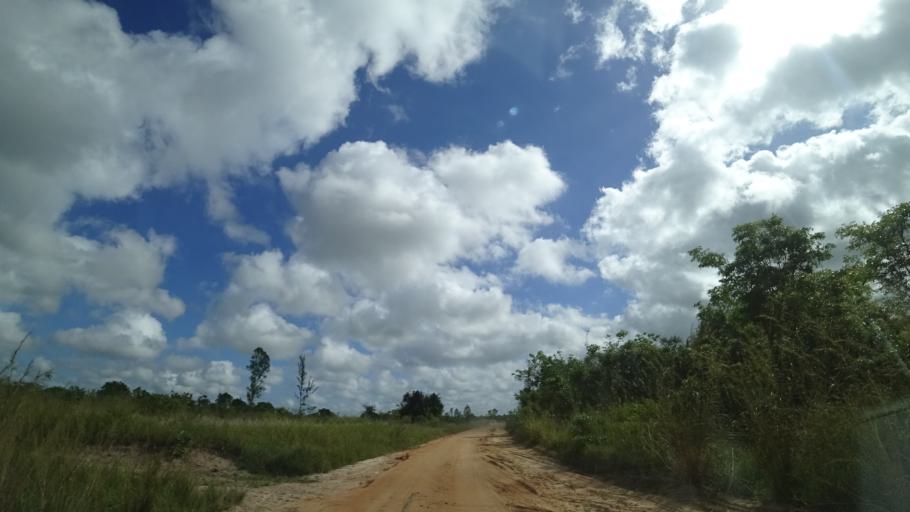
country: MZ
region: Sofala
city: Dondo
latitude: -19.4297
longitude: 34.7085
